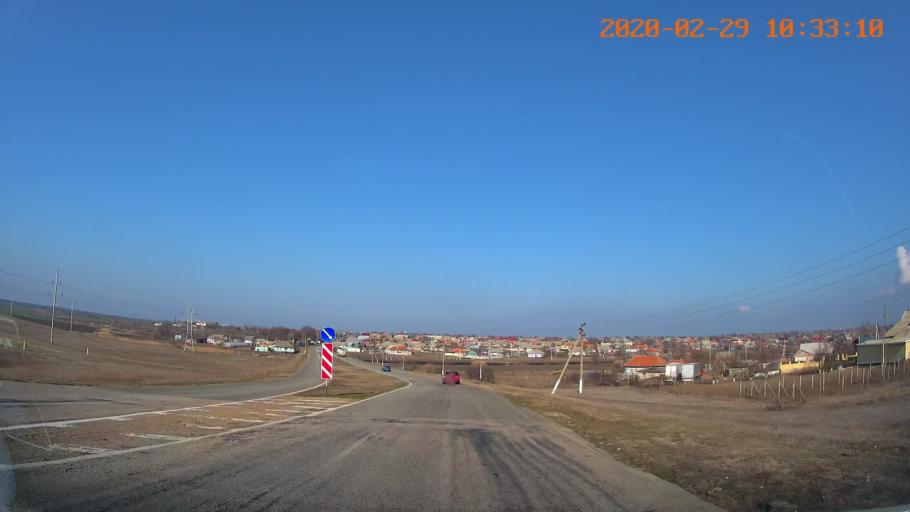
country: MD
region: Anenii Noi
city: Varnita
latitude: 46.9689
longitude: 29.5477
